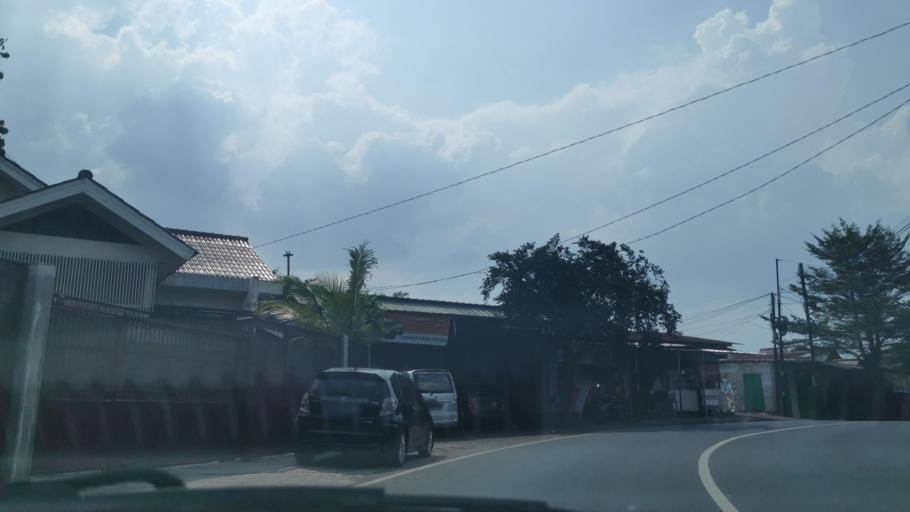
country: ID
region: West Java
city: Depok
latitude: -6.4078
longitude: 106.8349
